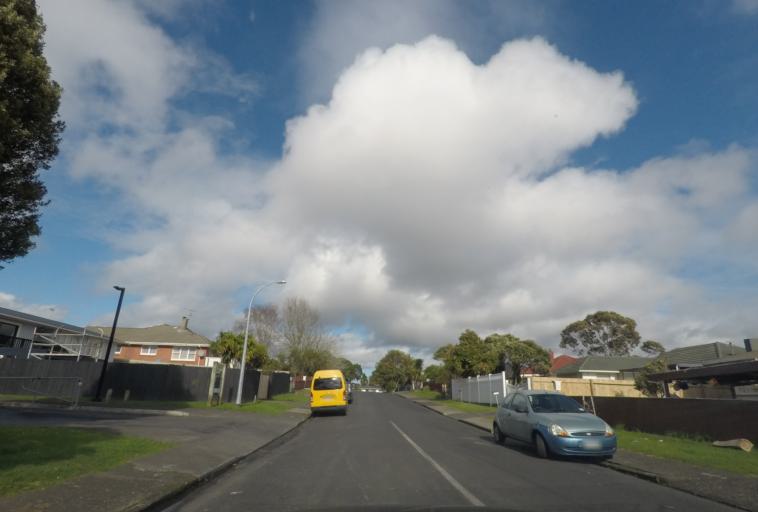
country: NZ
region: Auckland
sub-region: Auckland
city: Rosebank
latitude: -36.8949
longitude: 174.6626
